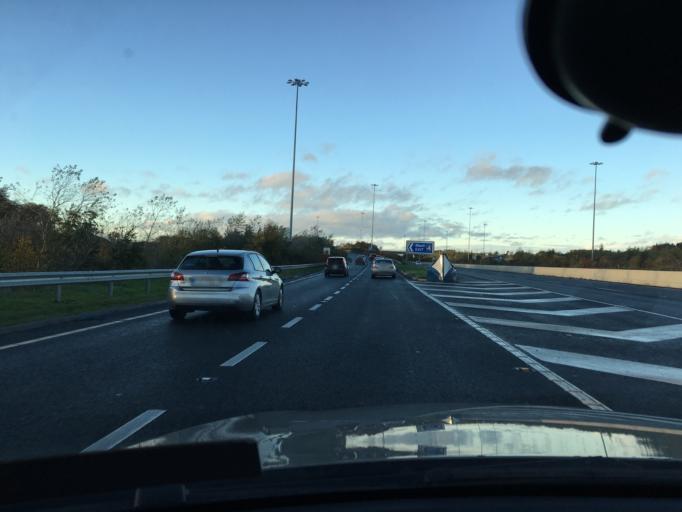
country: IE
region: Leinster
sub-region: Fingal County
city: Swords
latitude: 53.4736
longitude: -6.2034
